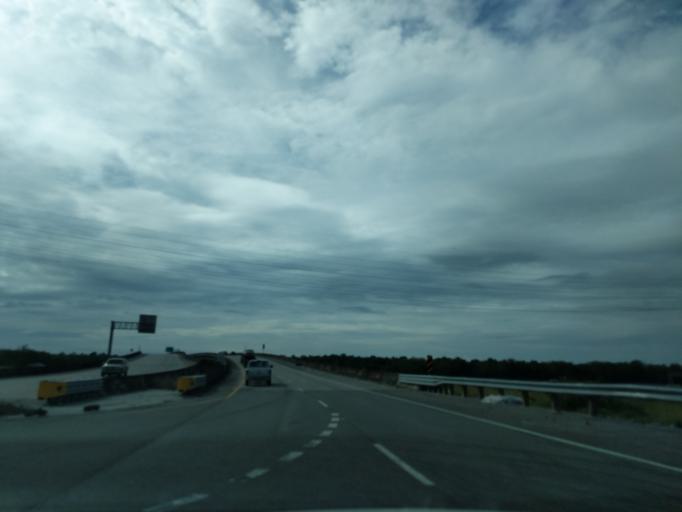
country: US
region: Louisiana
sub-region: Saint Bernard Parish
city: Chalmette
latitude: 30.0177
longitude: -89.9368
